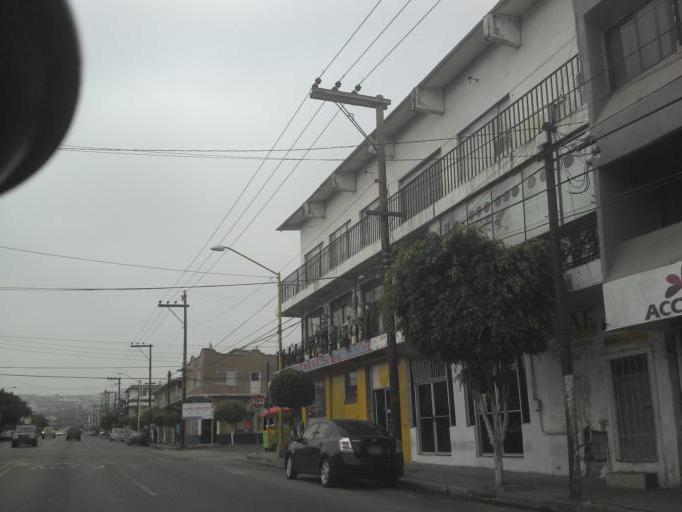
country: MX
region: Baja California
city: Tijuana
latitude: 32.5303
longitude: -117.0316
